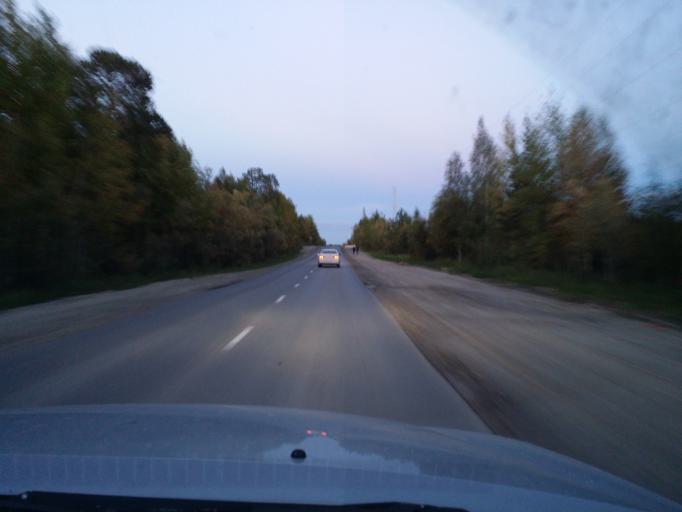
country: RU
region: Khanty-Mansiyskiy Avtonomnyy Okrug
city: Nizhnevartovsk
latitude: 60.9928
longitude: 76.4149
